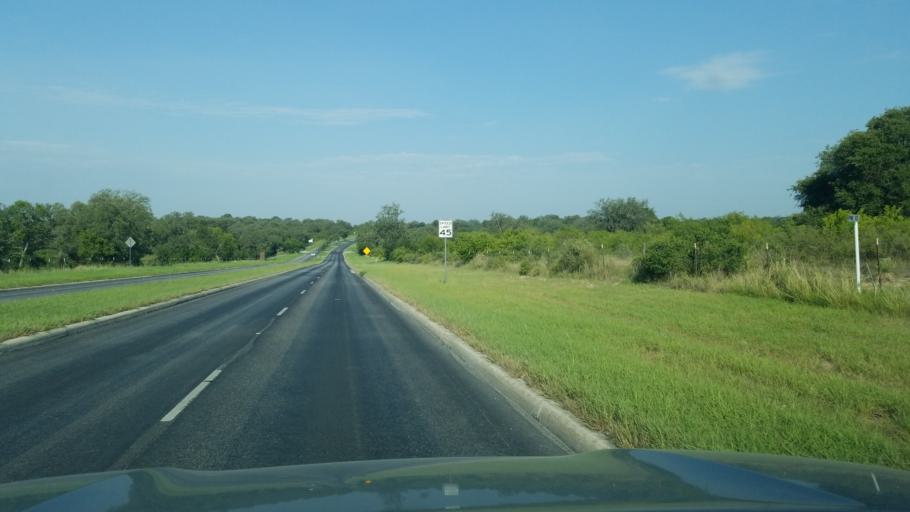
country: US
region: Texas
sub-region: Bexar County
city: Leon Valley
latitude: 29.4609
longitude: -98.7346
